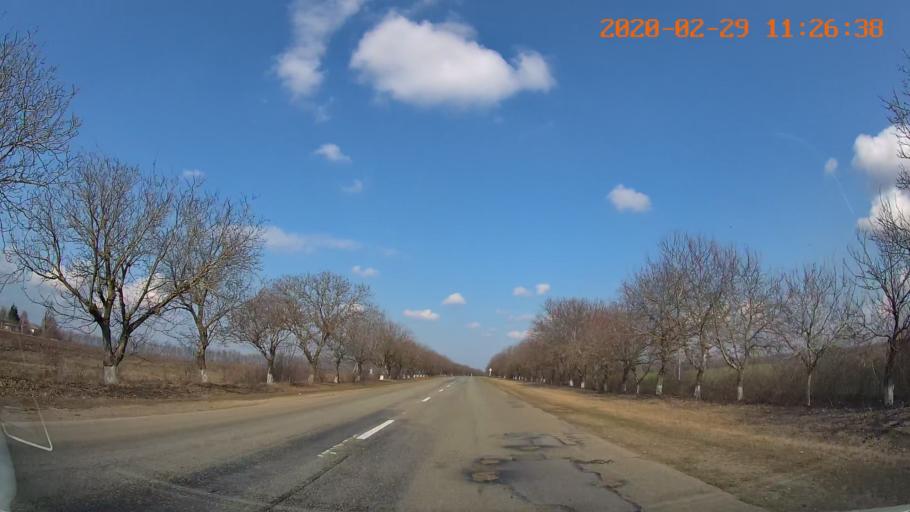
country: MD
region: Telenesti
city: Cocieri
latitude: 47.4559
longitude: 29.1452
